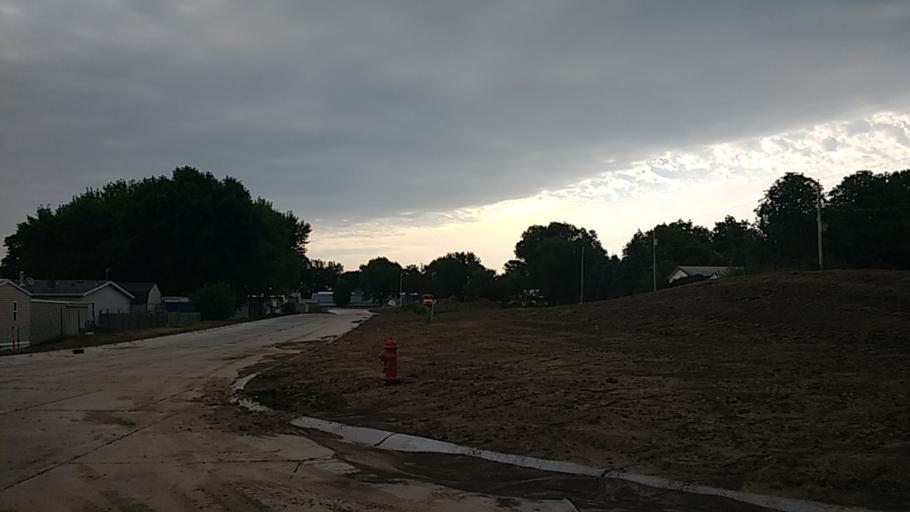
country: US
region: Iowa
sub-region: Woodbury County
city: Moville
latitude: 42.4875
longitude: -96.0679
